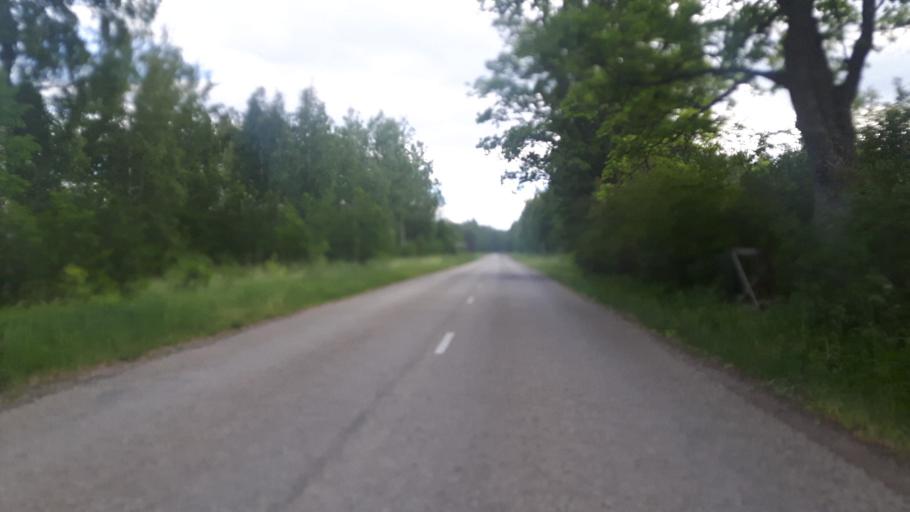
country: LV
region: Engure
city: Smarde
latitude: 57.0316
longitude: 23.3625
